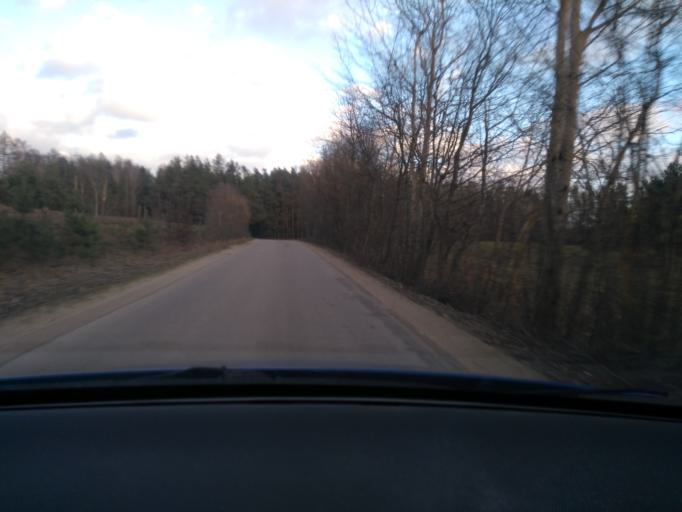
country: PL
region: Pomeranian Voivodeship
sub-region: Powiat kartuski
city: Przodkowo
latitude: 54.4130
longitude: 18.2568
